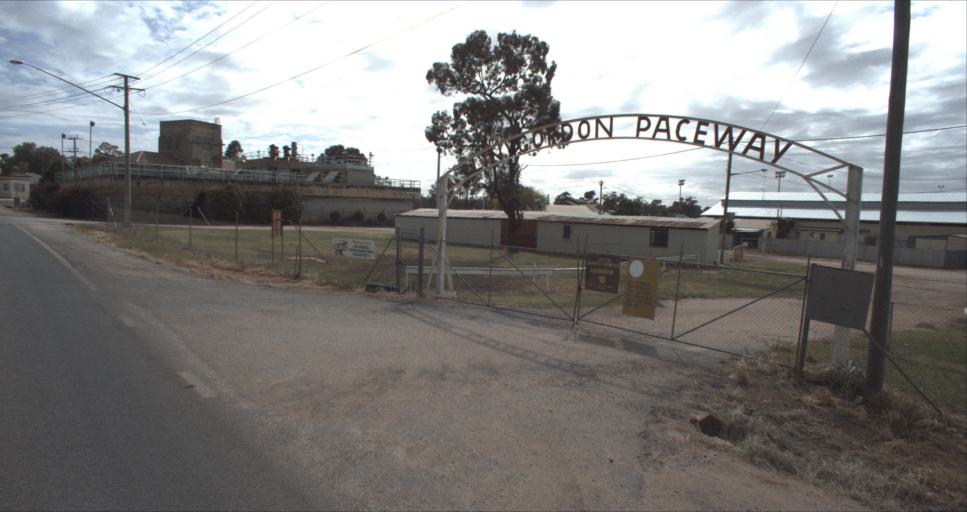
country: AU
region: New South Wales
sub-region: Leeton
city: Leeton
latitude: -34.5592
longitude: 146.4027
